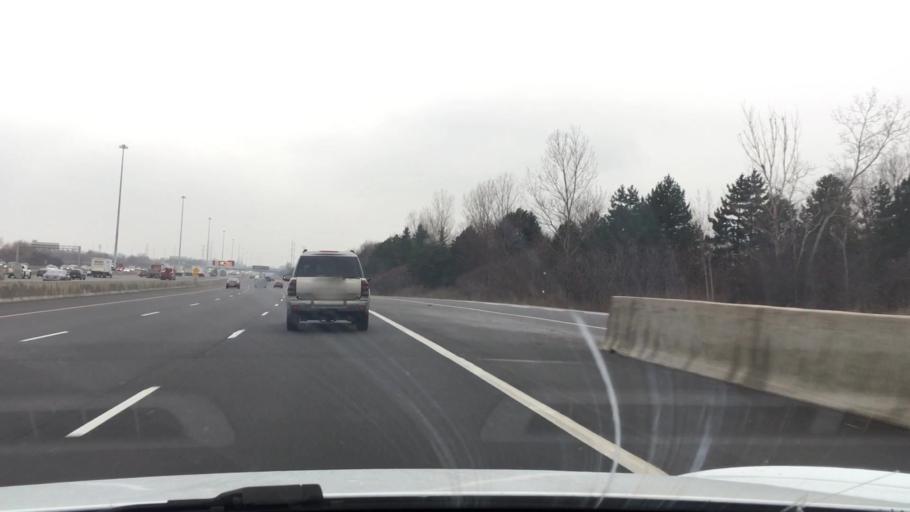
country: CA
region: Ontario
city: Scarborough
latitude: 43.8004
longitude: -79.1729
